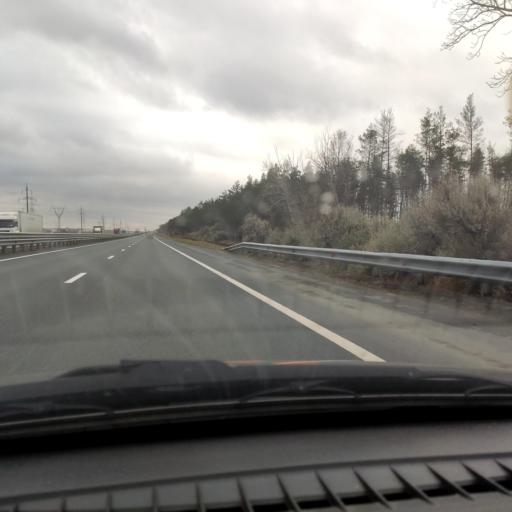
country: RU
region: Samara
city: Povolzhskiy
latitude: 53.5144
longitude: 49.6313
